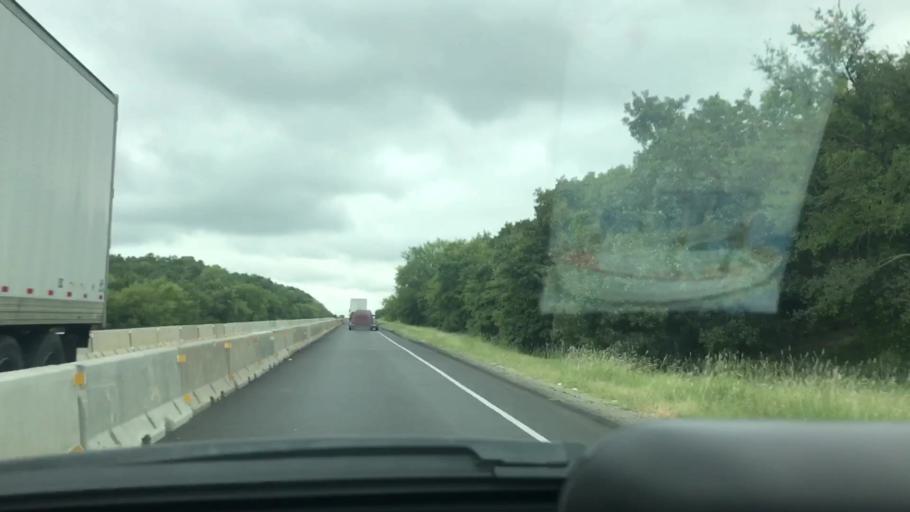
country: US
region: Oklahoma
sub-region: McIntosh County
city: Eufaula
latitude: 35.2679
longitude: -95.5910
